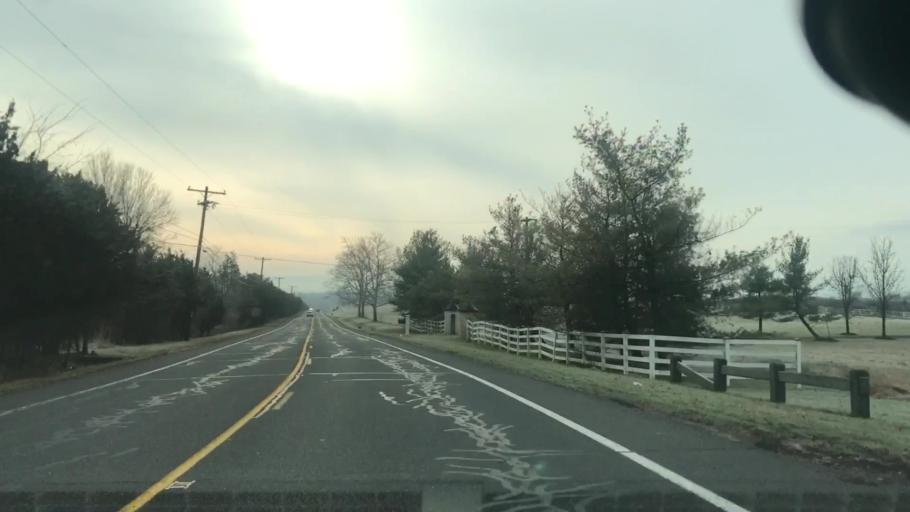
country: US
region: New Jersey
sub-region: Hunterdon County
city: Whitehouse Station
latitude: 40.6343
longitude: -74.7117
